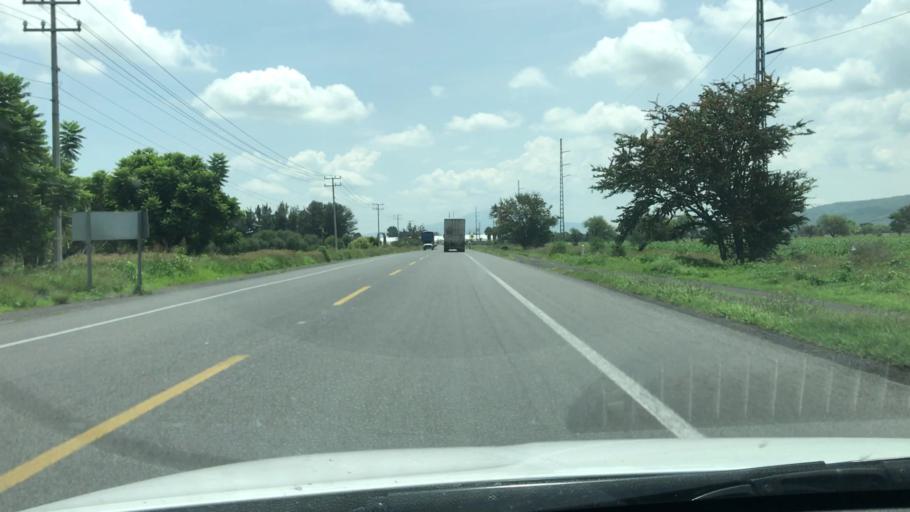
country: MX
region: Michoacan
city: Tanhuato de Guerrero
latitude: 20.2819
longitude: -102.3485
